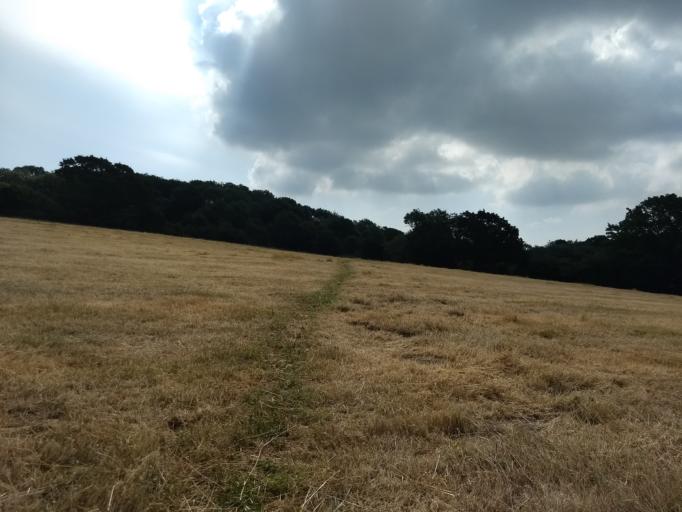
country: GB
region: England
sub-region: Isle of Wight
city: Ryde
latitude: 50.7105
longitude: -1.1526
